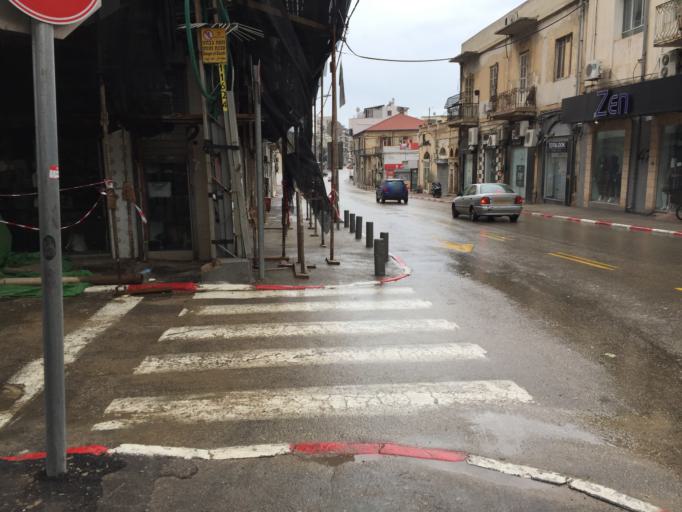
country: IL
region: Tel Aviv
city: Yafo
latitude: 32.0587
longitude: 34.7656
